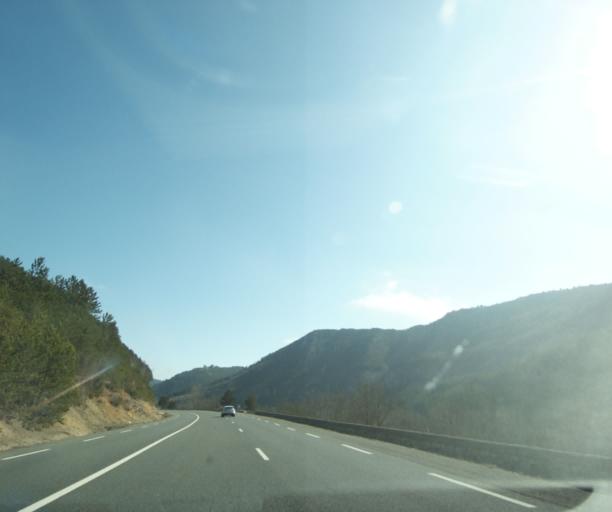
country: FR
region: Languedoc-Roussillon
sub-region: Departement de la Lozere
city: Mende
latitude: 44.4798
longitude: 3.4317
